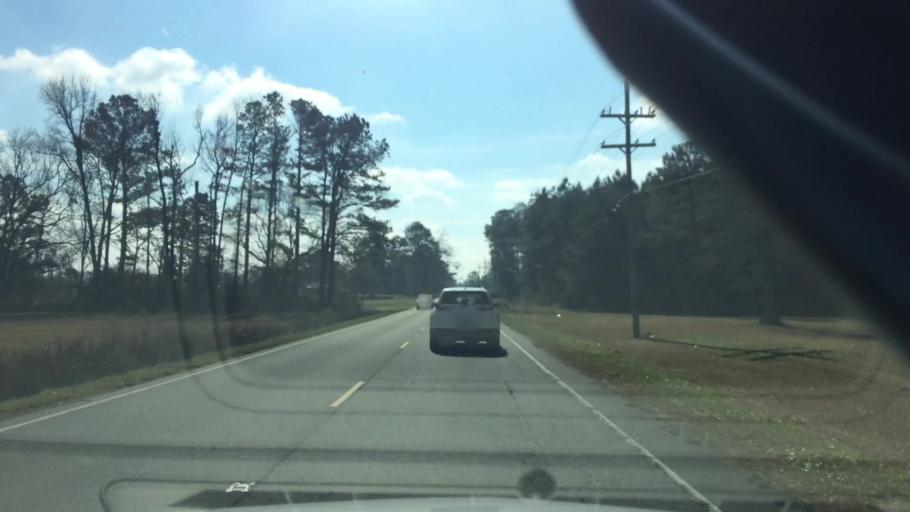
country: US
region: North Carolina
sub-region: Duplin County
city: Beulaville
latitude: 34.8985
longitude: -77.7810
